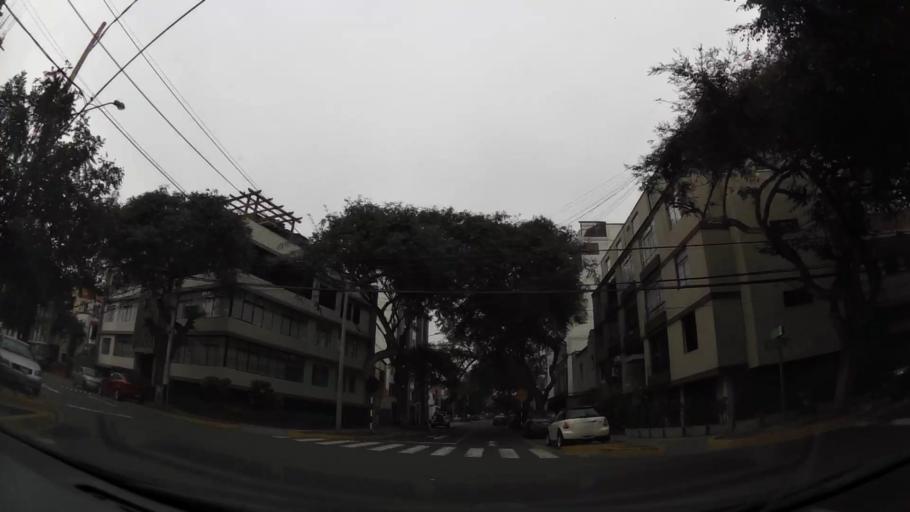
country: PE
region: Lima
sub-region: Lima
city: Surco
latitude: -12.1317
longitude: -77.0276
